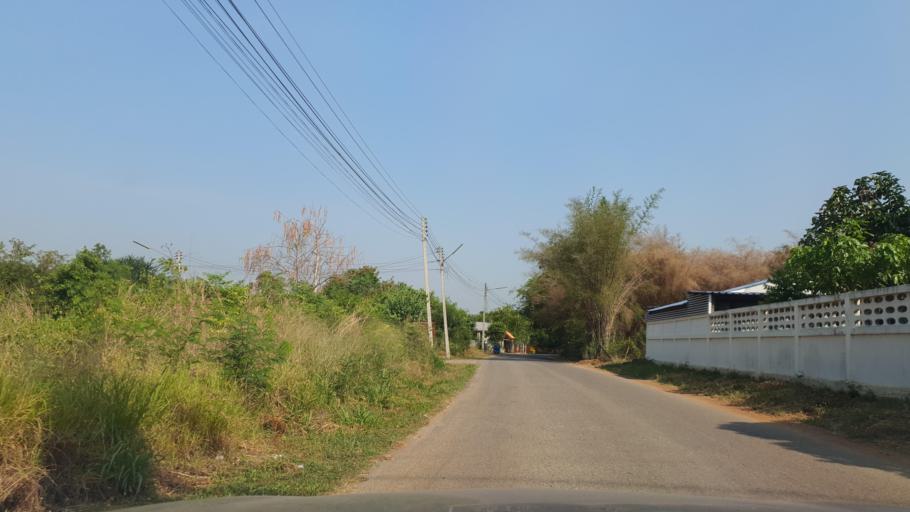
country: TH
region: Kanchanaburi
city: Kanchanaburi
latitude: 14.0687
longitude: 99.4855
